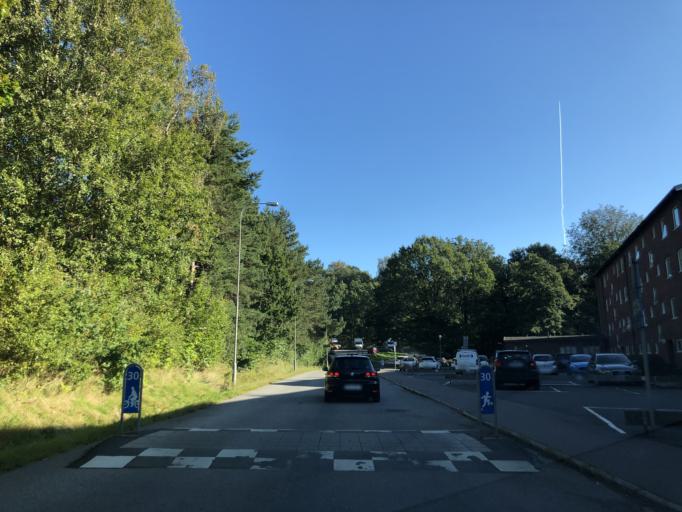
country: SE
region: Vaestra Goetaland
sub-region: Molndal
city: Moelndal
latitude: 57.6827
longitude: 12.0157
